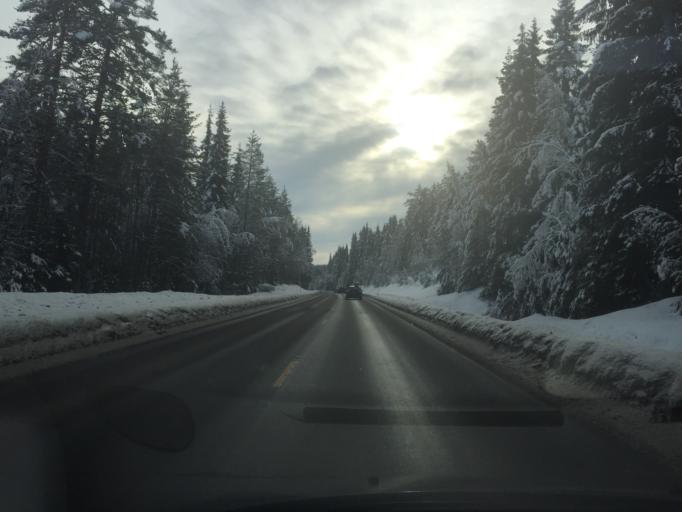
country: NO
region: Hedmark
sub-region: Trysil
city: Innbygda
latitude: 61.2796
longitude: 12.2851
